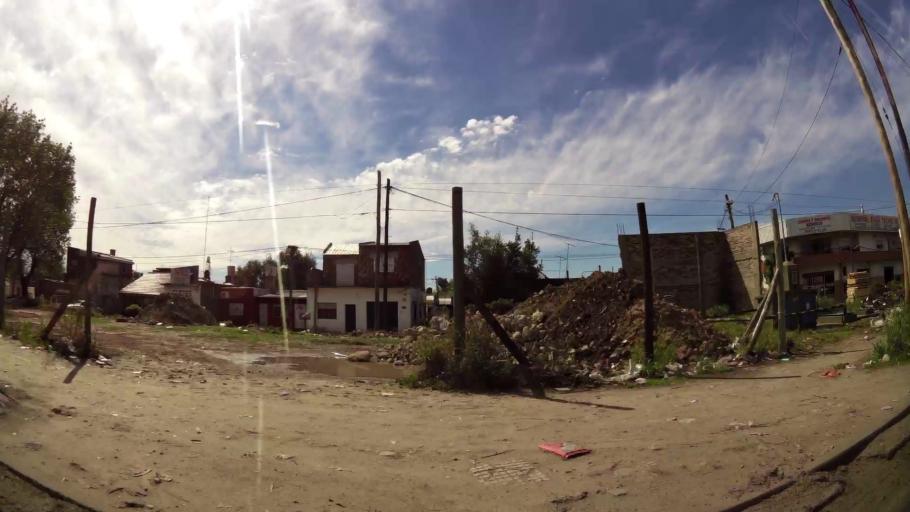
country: AR
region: Buenos Aires
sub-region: Partido de Almirante Brown
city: Adrogue
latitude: -34.7906
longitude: -58.3102
